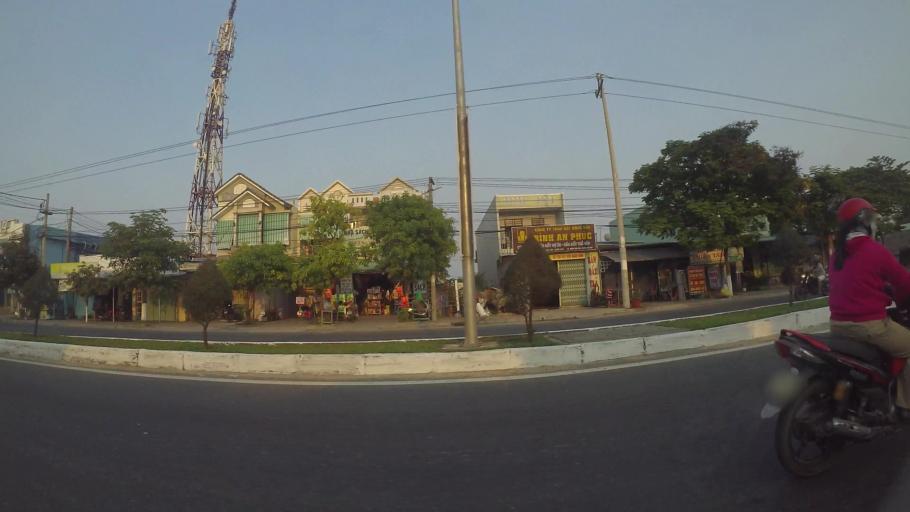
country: VN
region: Da Nang
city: Ngu Hanh Son
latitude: 15.9548
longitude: 108.2546
